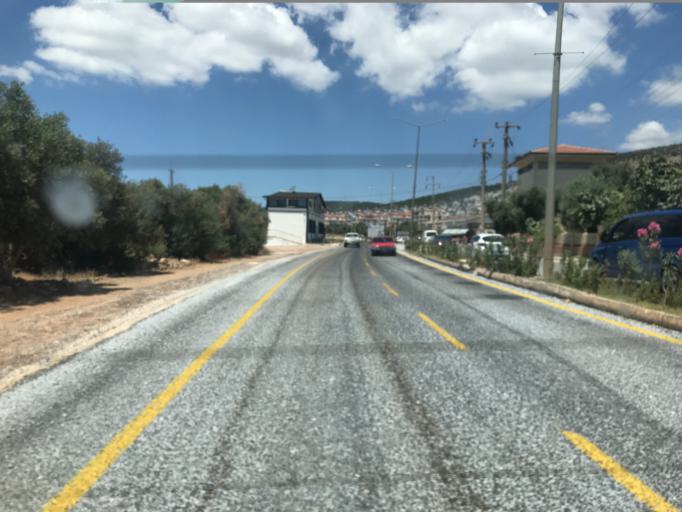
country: TR
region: Aydin
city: Sarikemer
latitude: 37.4153
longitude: 27.4196
